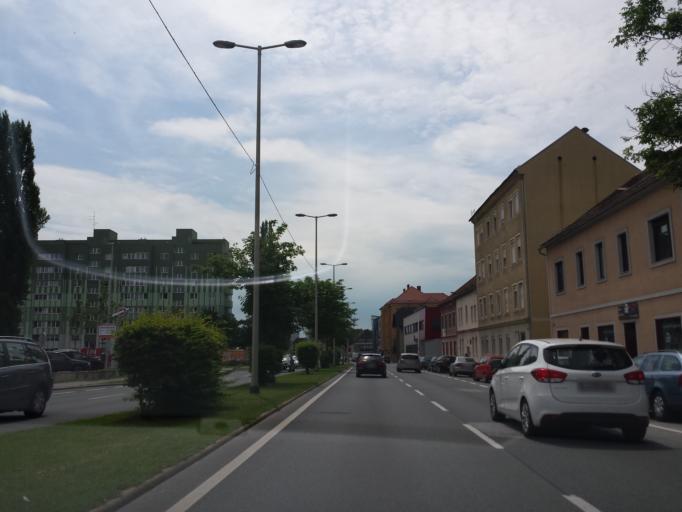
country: AT
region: Styria
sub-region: Graz Stadt
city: Goesting
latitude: 47.0954
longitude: 15.4047
